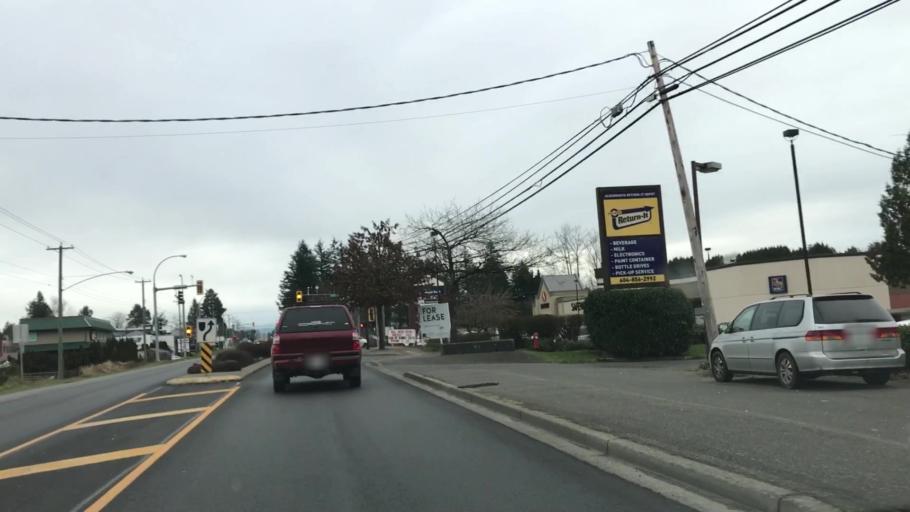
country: CA
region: British Columbia
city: Aldergrove
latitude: 49.0577
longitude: -122.4636
